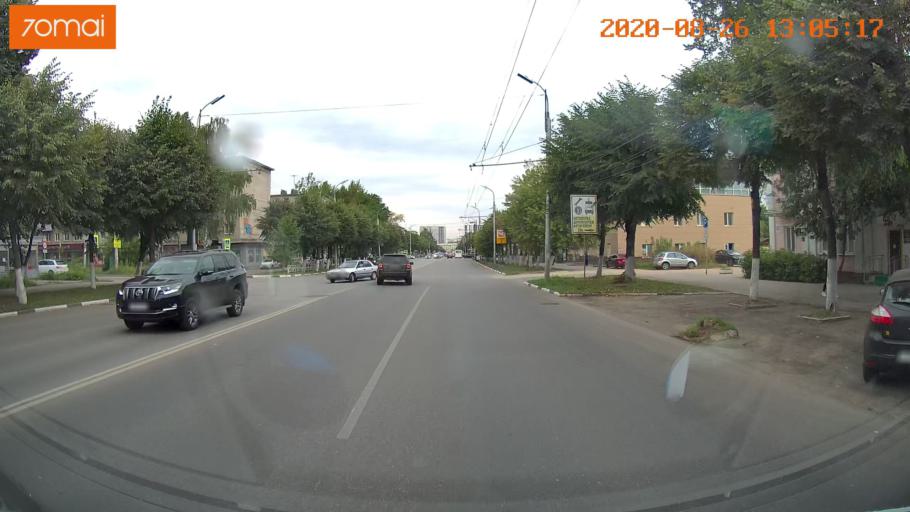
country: RU
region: Rjazan
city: Ryazan'
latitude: 54.6186
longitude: 39.7270
